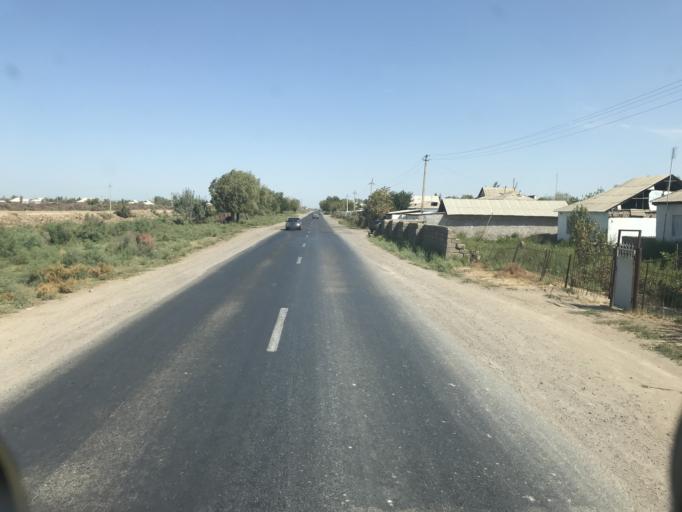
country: KZ
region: Ongtustik Qazaqstan
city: Ilyich
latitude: 40.7643
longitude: 68.5372
